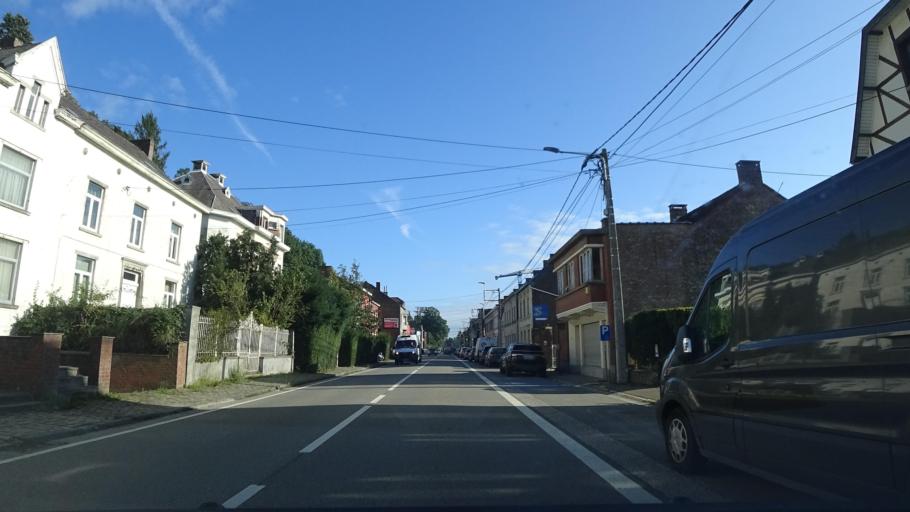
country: BE
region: Wallonia
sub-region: Province du Brabant Wallon
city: Court-Saint-Etienne
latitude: 50.6465
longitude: 4.5623
